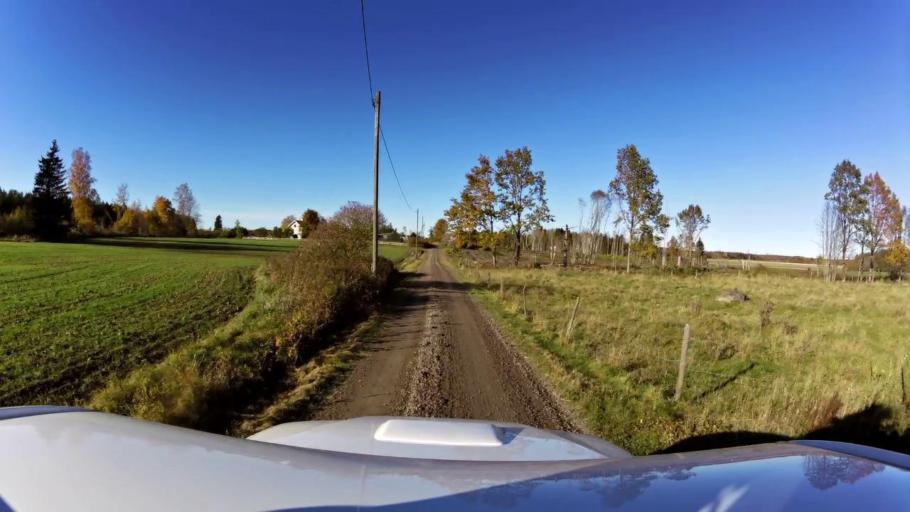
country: SE
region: OEstergoetland
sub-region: Linkopings Kommun
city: Ljungsbro
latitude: 58.5135
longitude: 15.4067
